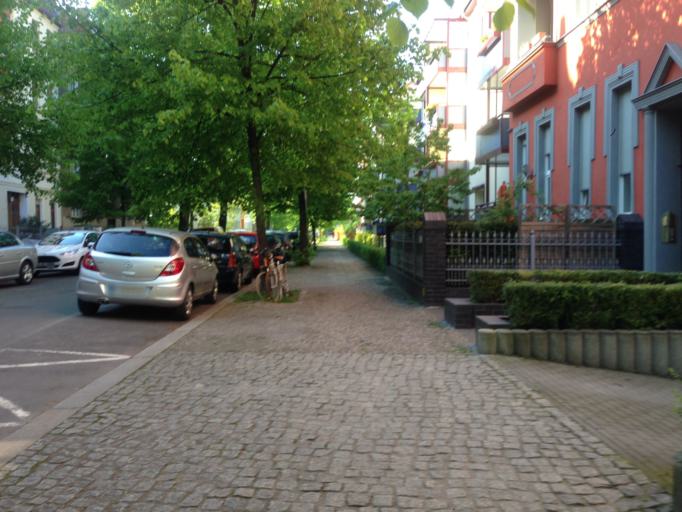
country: DE
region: Berlin
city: Niederschonhausen
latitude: 52.5767
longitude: 13.4181
